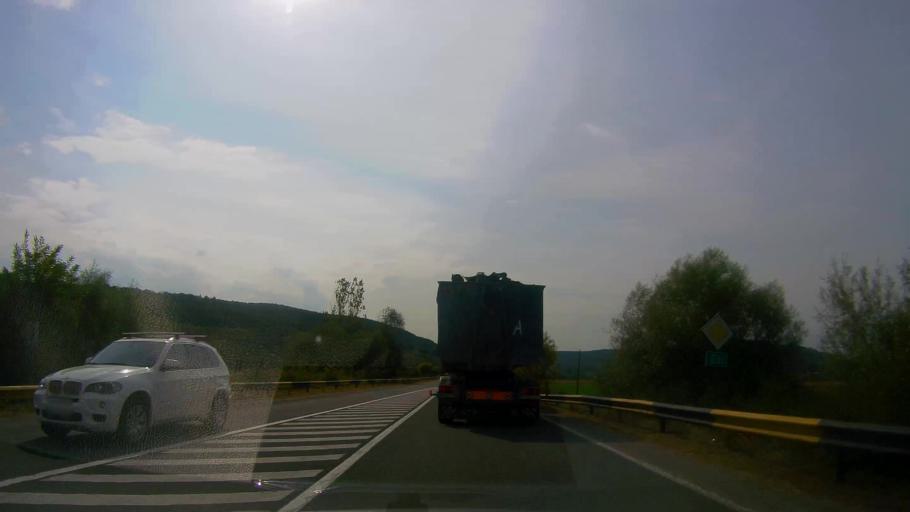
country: RO
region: Salaj
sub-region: Comuna Zimbor
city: Zimbor
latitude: 46.9944
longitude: 23.2500
